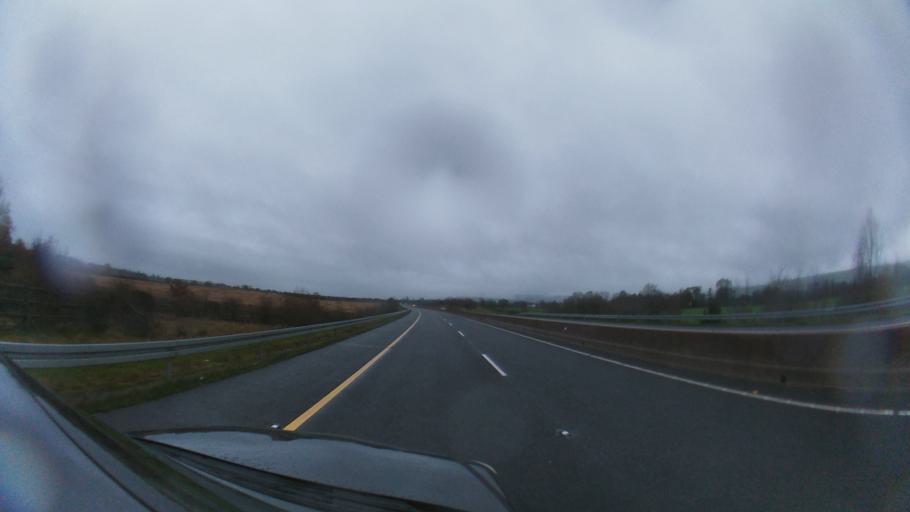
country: IE
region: Leinster
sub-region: County Carlow
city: Bagenalstown
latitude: 52.7571
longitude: -6.9869
